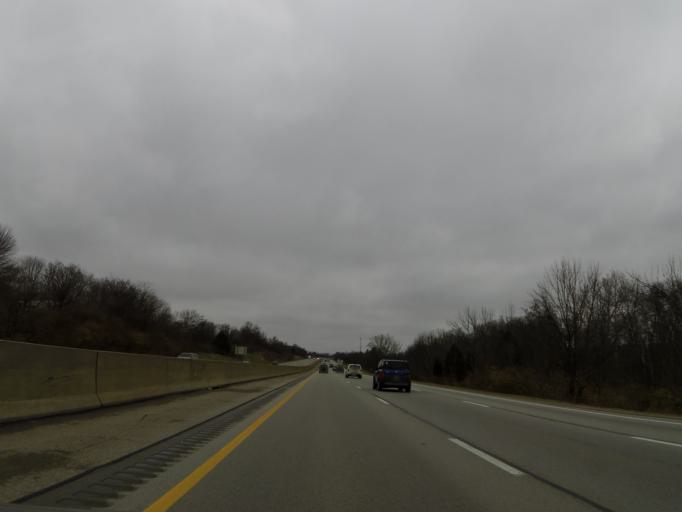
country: US
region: Kentucky
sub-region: Boone County
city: Walton
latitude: 38.8406
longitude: -84.6159
